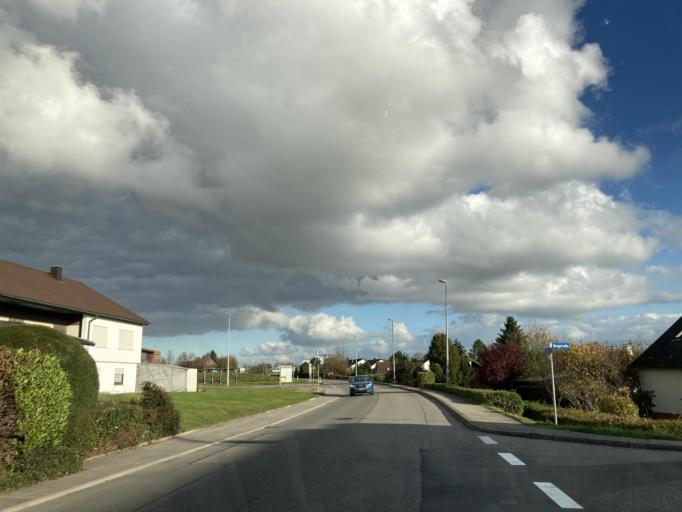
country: DE
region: Baden-Wuerttemberg
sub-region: Karlsruhe Region
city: Empfingen
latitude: 48.3948
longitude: 8.7142
